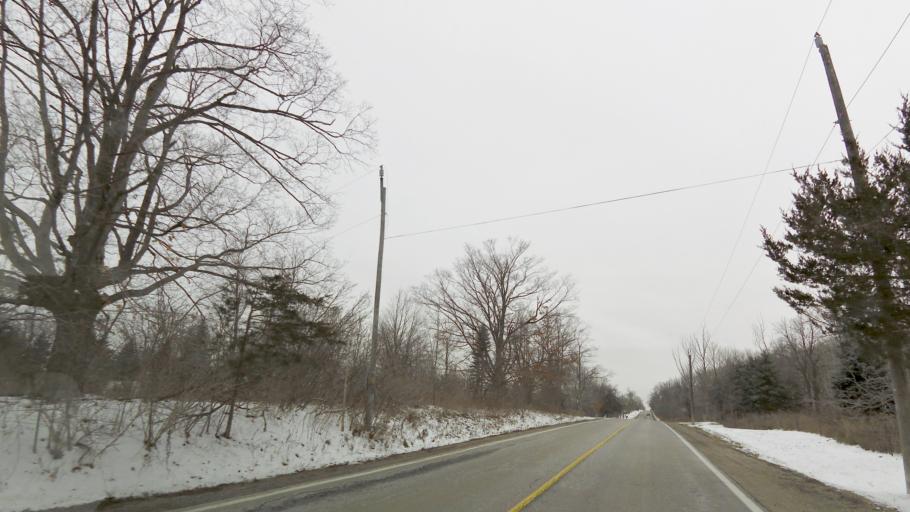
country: CA
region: Ontario
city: Vaughan
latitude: 43.8809
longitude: -79.5958
